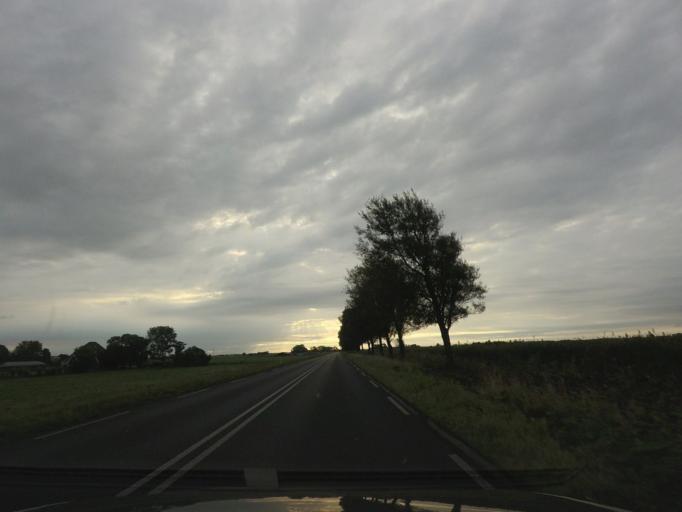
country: NL
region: North Holland
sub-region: Gemeente Uitgeest
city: Uitgeest
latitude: 52.5616
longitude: 4.7627
